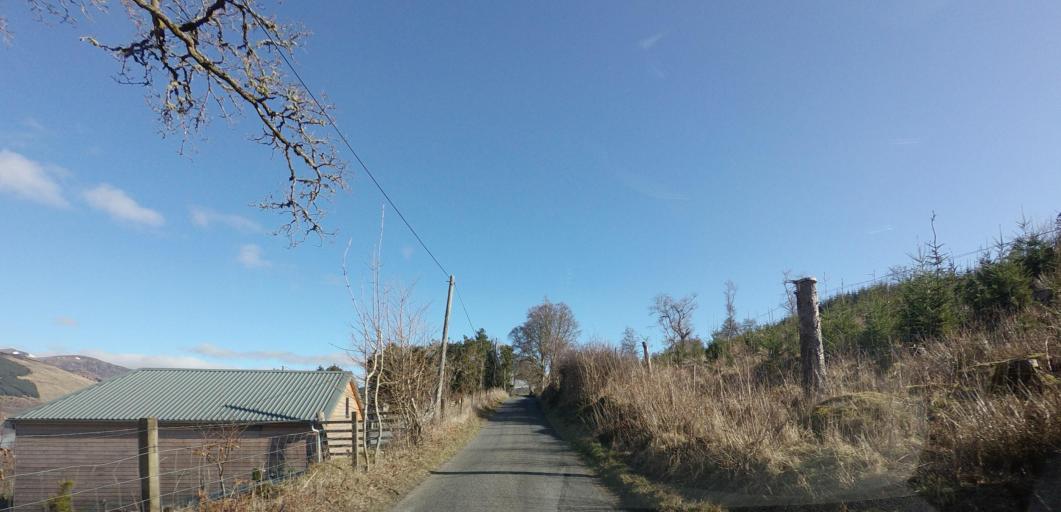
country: GB
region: Scotland
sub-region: Perth and Kinross
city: Comrie
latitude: 56.5542
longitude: -4.0860
